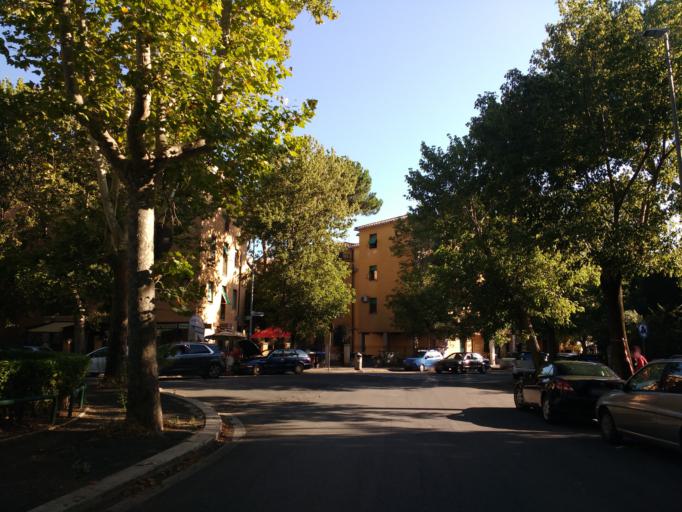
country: IT
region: Latium
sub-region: Citta metropolitana di Roma Capitale
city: Acilia-Castel Fusano-Ostia Antica
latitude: 41.7779
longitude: 12.3551
